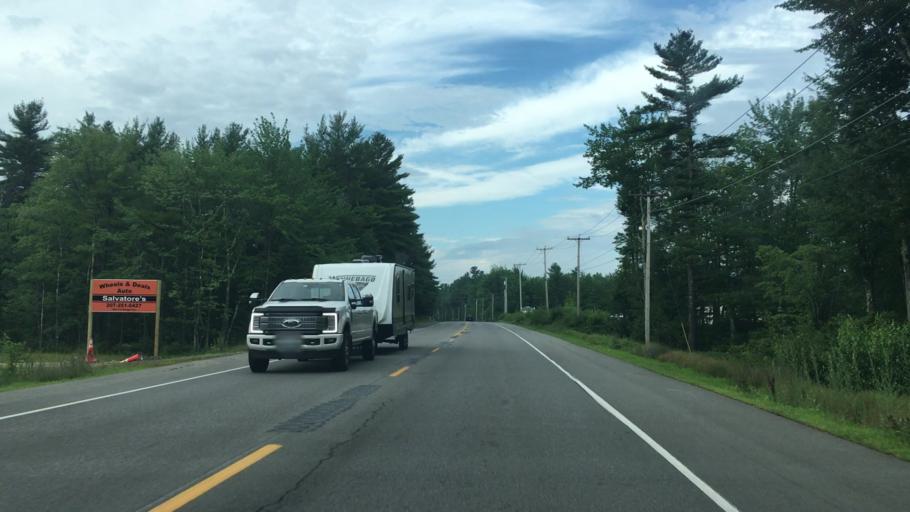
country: US
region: Maine
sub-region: York County
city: Lebanon
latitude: 43.3639
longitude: -70.9083
